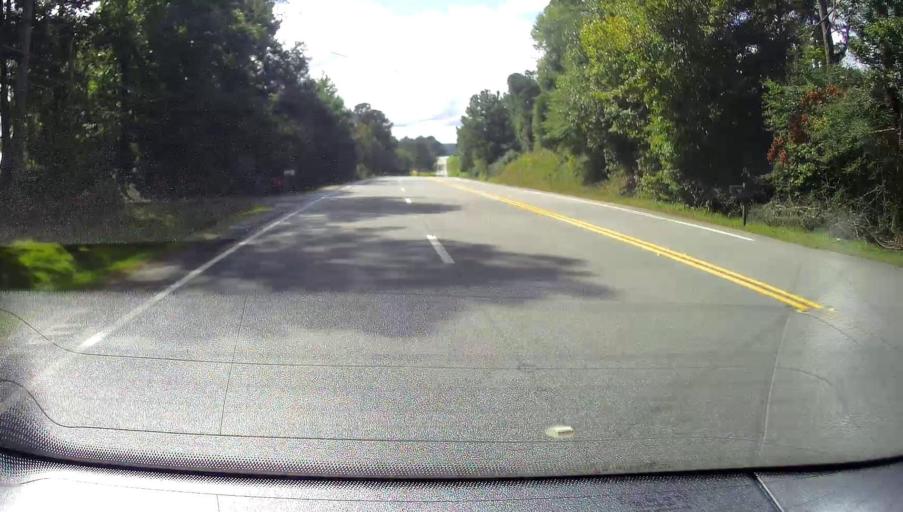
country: US
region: Georgia
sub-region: Baldwin County
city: Milledgeville
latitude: 33.0423
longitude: -83.2973
